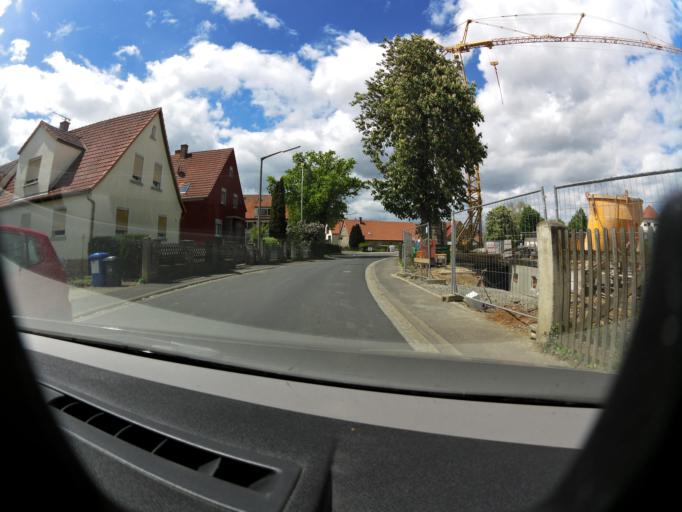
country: DE
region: Bavaria
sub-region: Regierungsbezirk Unterfranken
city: Buchbrunn
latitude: 49.7591
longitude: 10.1392
